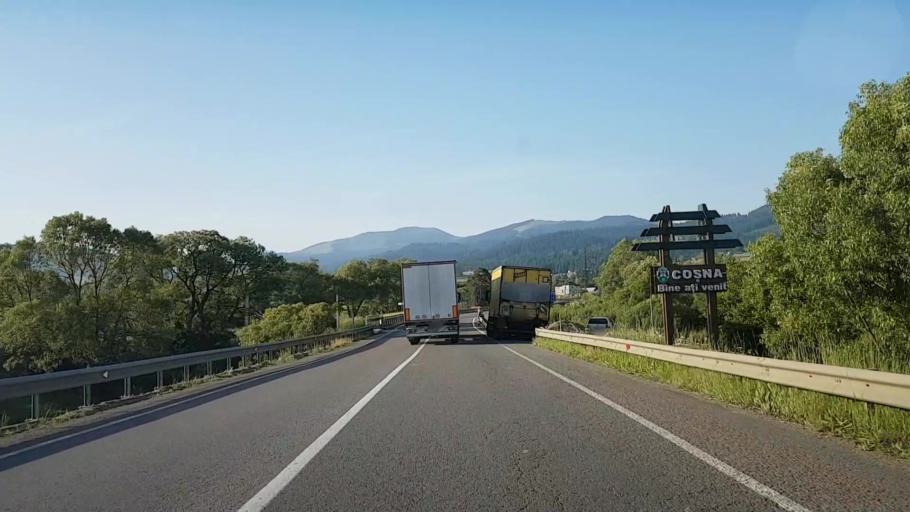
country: RO
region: Suceava
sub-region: Comuna Cosna
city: Cosna
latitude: 47.3581
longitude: 25.1888
